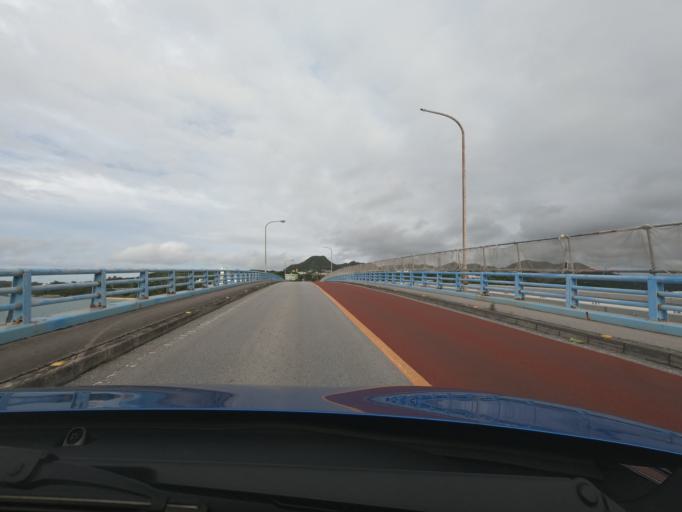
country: JP
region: Okinawa
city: Nago
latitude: 26.6605
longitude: 127.8886
